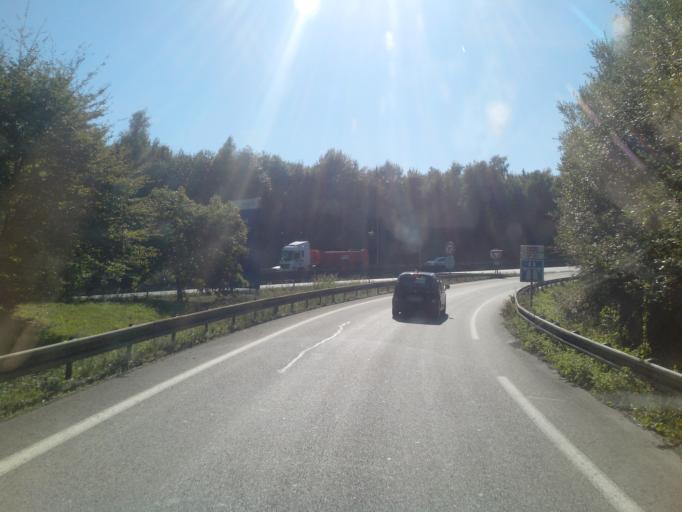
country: FR
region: Pays de la Loire
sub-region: Departement de la Loire-Atlantique
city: La Chapelle-sur-Erdre
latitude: 47.2685
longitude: -1.5638
